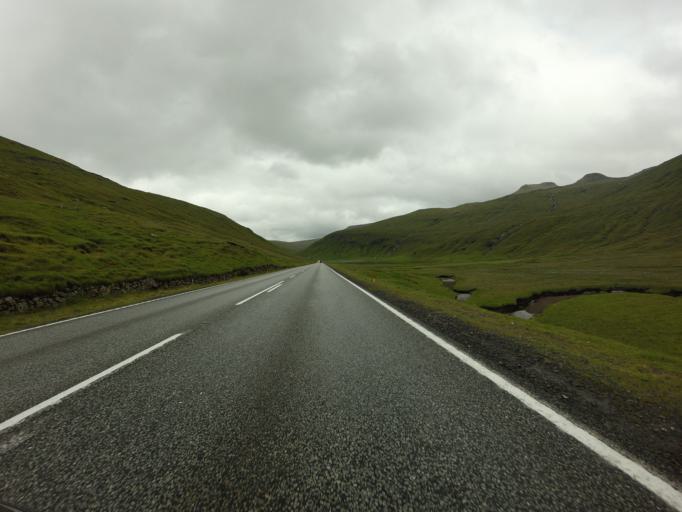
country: FO
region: Streymoy
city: Kollafjordhur
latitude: 62.1216
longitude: -6.9891
